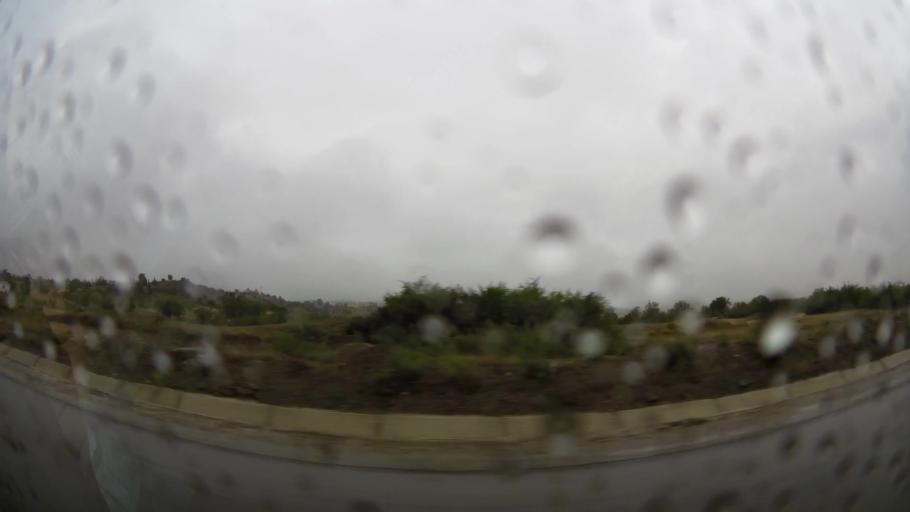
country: MA
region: Oriental
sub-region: Nador
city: Midar
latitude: 34.8655
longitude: -3.7244
